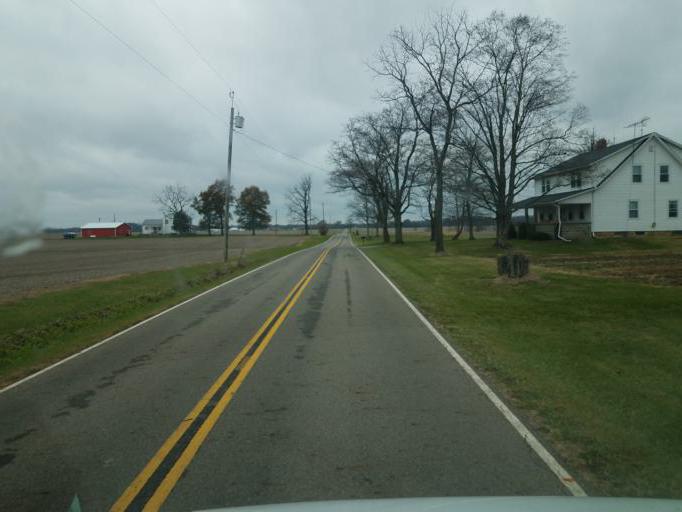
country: US
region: Ohio
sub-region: Licking County
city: Johnstown
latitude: 40.2211
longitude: -82.6285
